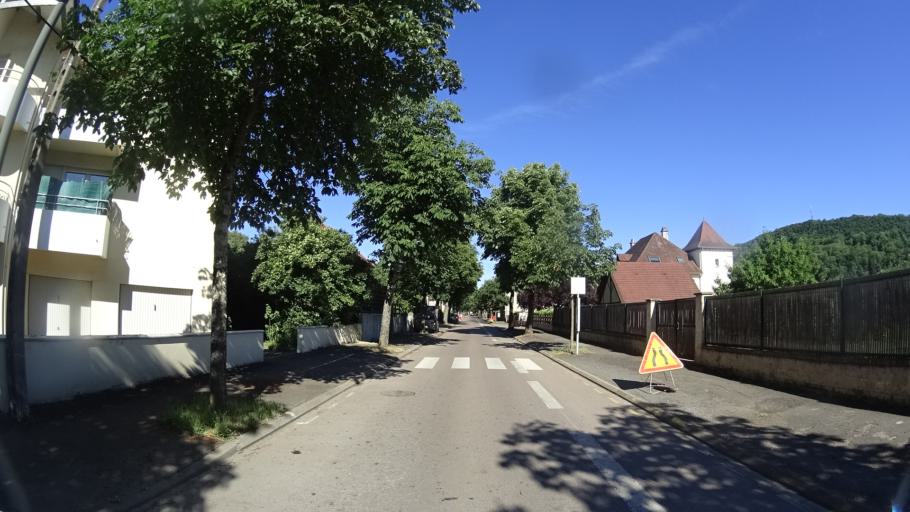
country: FR
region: Midi-Pyrenees
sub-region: Departement du Lot
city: Figeac
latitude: 44.6089
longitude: 2.0205
